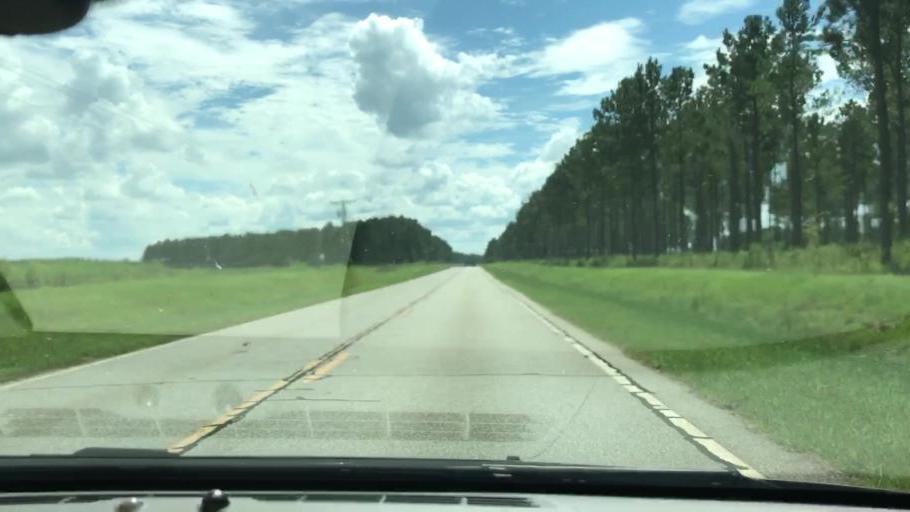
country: US
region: Georgia
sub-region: Quitman County
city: Georgetown
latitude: 32.0653
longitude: -85.0362
